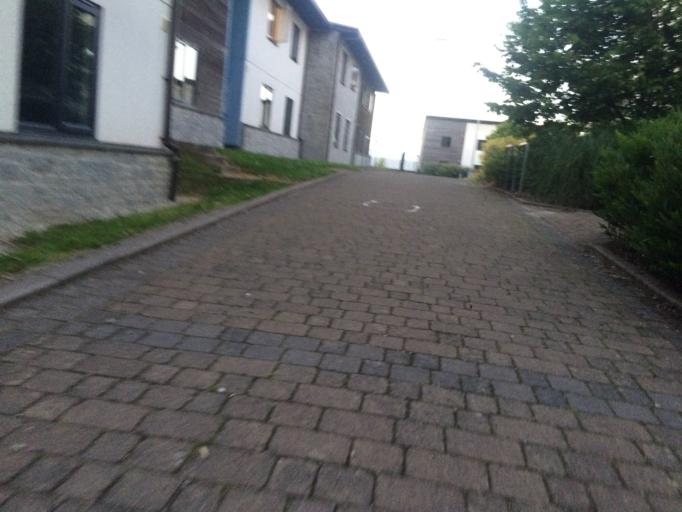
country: GB
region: England
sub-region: Cornwall
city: Penryn
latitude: 50.1719
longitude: -5.1214
